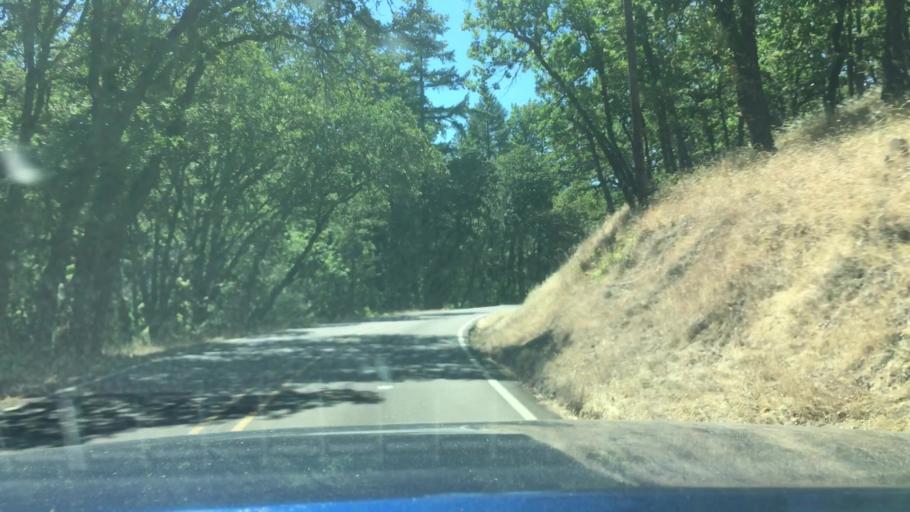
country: US
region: Oregon
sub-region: Douglas County
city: Winston
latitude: 43.1432
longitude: -123.4177
